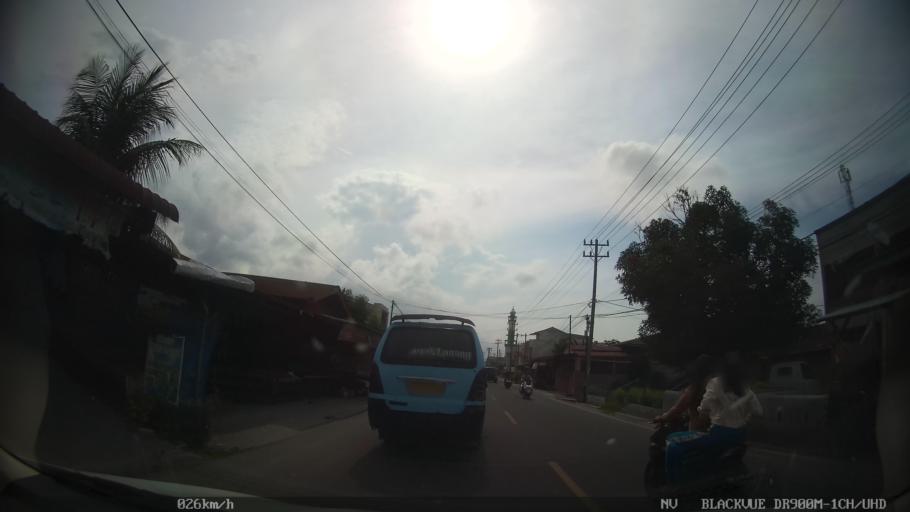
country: ID
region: North Sumatra
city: Percut
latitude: 3.6071
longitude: 98.7687
